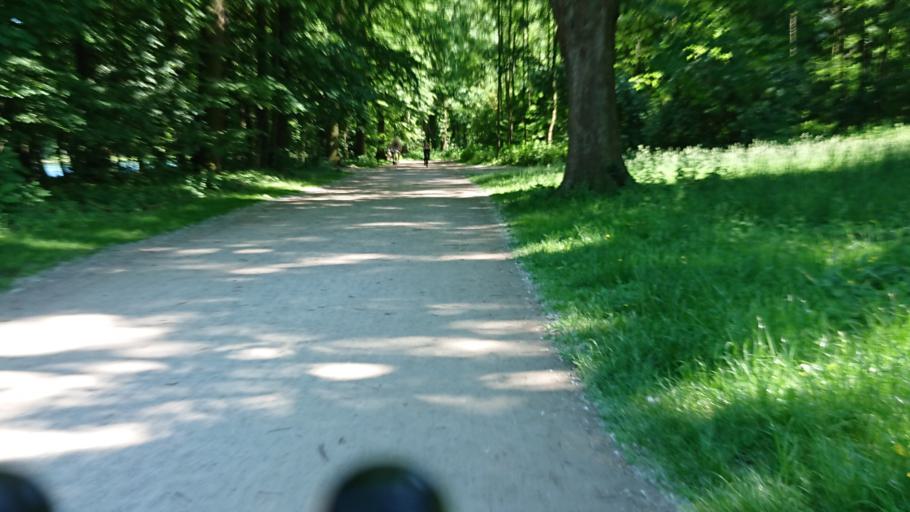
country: DE
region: North Rhine-Westphalia
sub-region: Regierungsbezirk Koln
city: Mengenich
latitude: 50.9296
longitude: 6.8766
